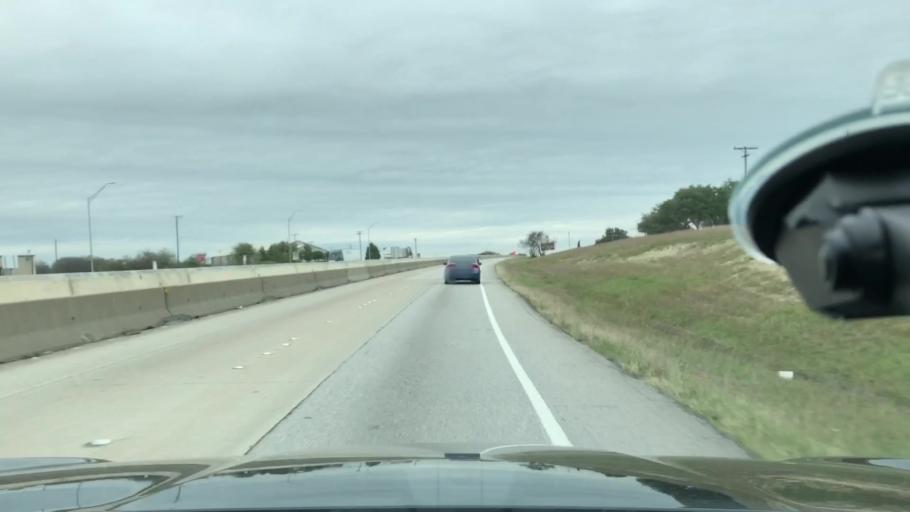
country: US
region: Texas
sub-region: Ellis County
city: Waxahachie
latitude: 32.4157
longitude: -96.8709
